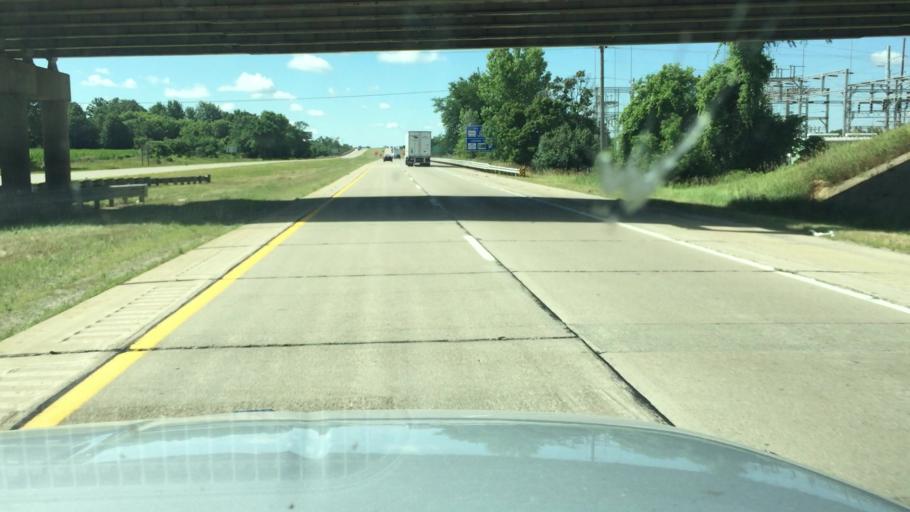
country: US
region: Michigan
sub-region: Eaton County
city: Charlotte
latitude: 42.5683
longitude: -84.8212
